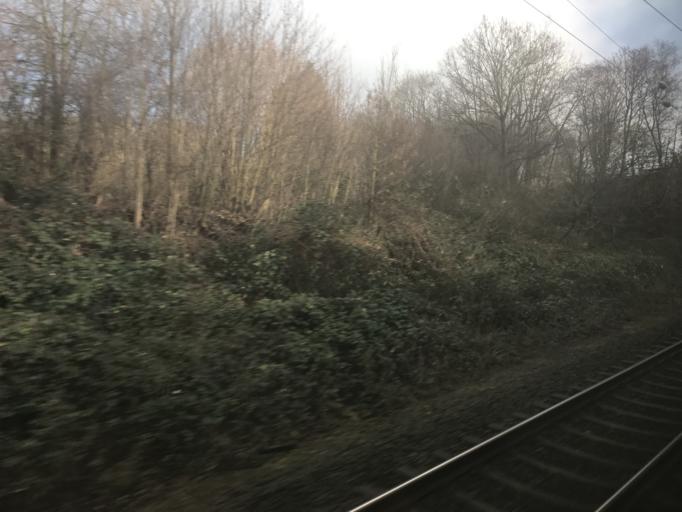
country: DE
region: North Rhine-Westphalia
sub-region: Regierungsbezirk Arnsberg
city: Bochum
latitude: 51.4856
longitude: 7.2887
